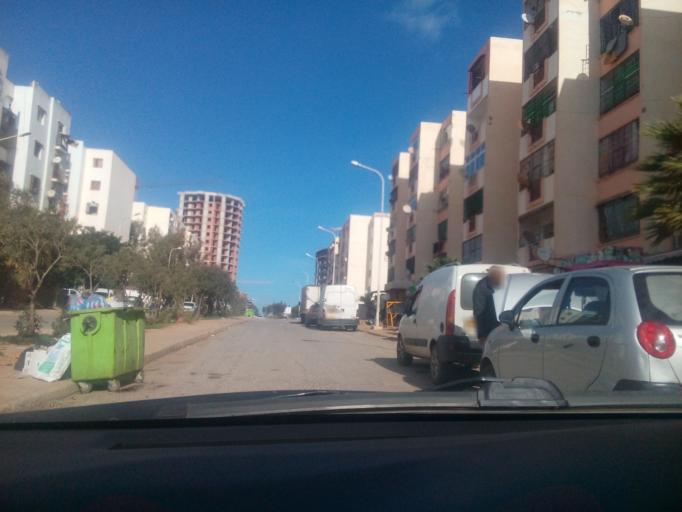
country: DZ
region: Oran
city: Bir el Djir
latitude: 35.7066
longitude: -0.5632
